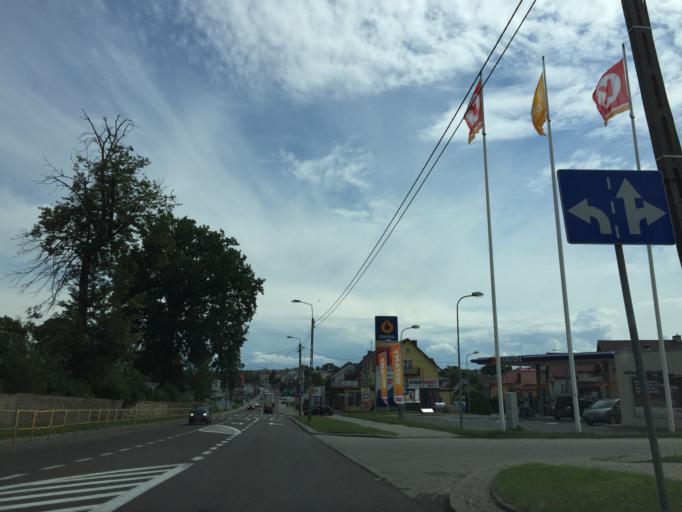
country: PL
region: Podlasie
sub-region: Powiat siemiatycki
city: Siemiatycze
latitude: 52.4323
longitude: 22.8603
